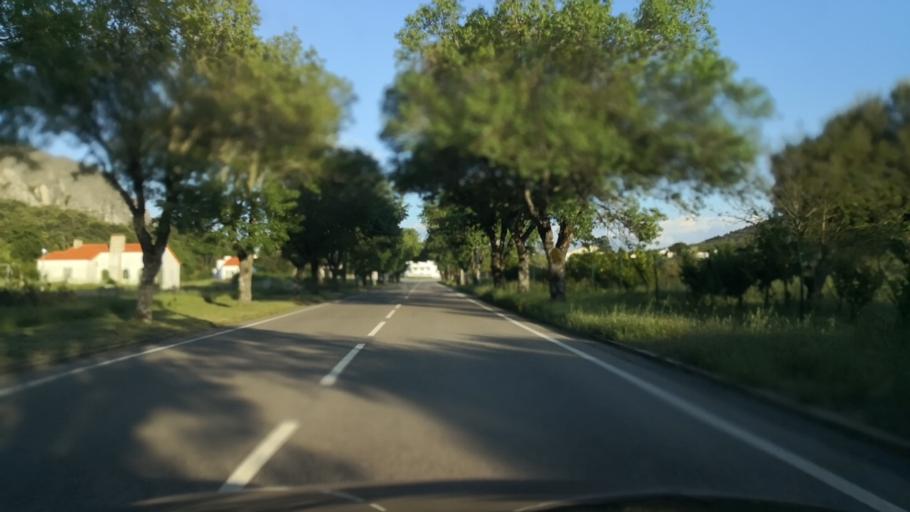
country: PT
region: Portalegre
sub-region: Portalegre
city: Sao Juliao
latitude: 39.3541
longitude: -7.3106
